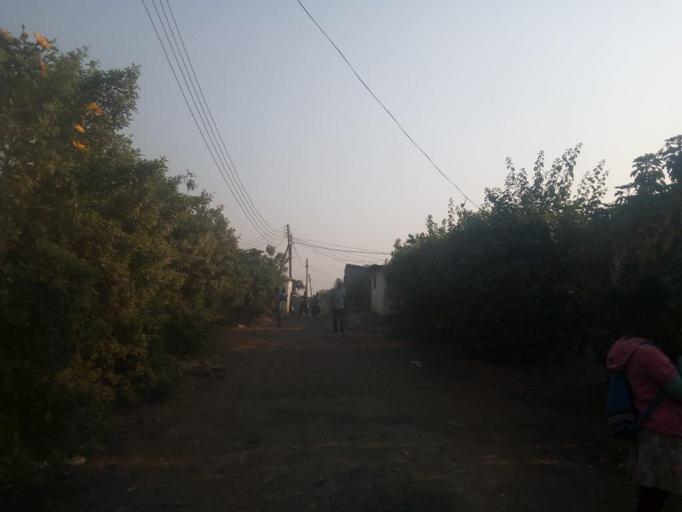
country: ZM
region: Lusaka
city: Lusaka
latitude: -15.4062
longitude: 28.3633
